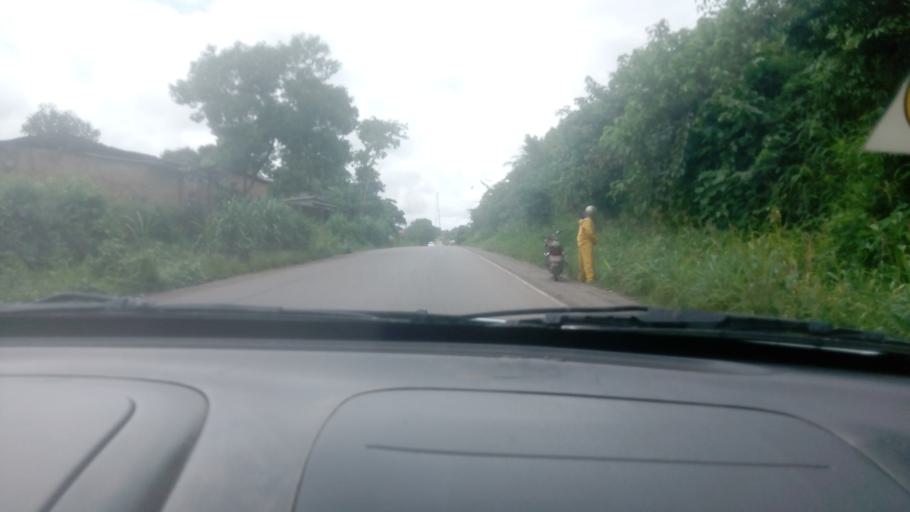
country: SL
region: Northern Province
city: Magburaka
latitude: 8.7294
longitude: -11.9438
